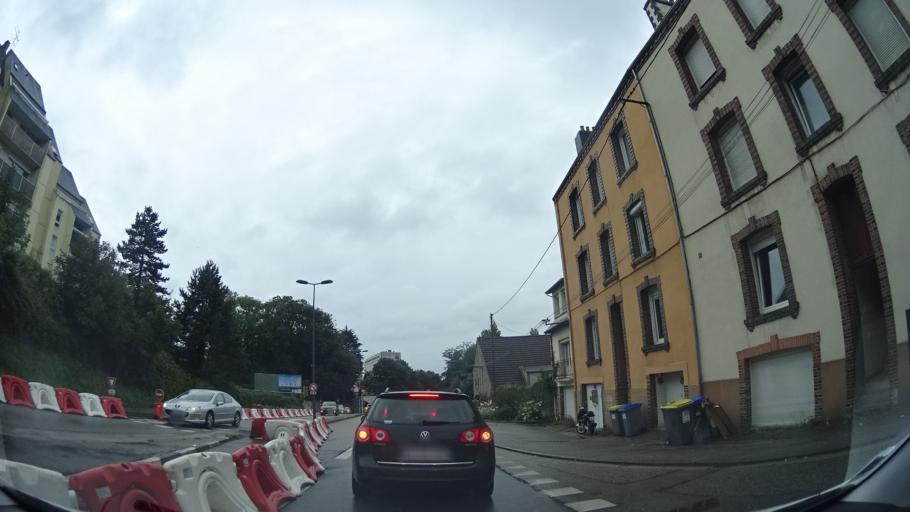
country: FR
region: Lower Normandy
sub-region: Departement de la Manche
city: Cherbourg-Octeville
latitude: 49.6316
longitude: -1.6238
